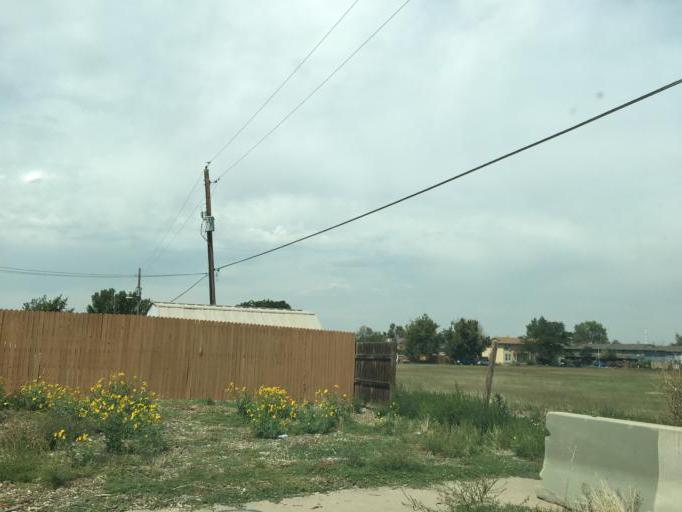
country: US
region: Colorado
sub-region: Adams County
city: Aurora
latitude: 39.7365
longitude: -104.7947
